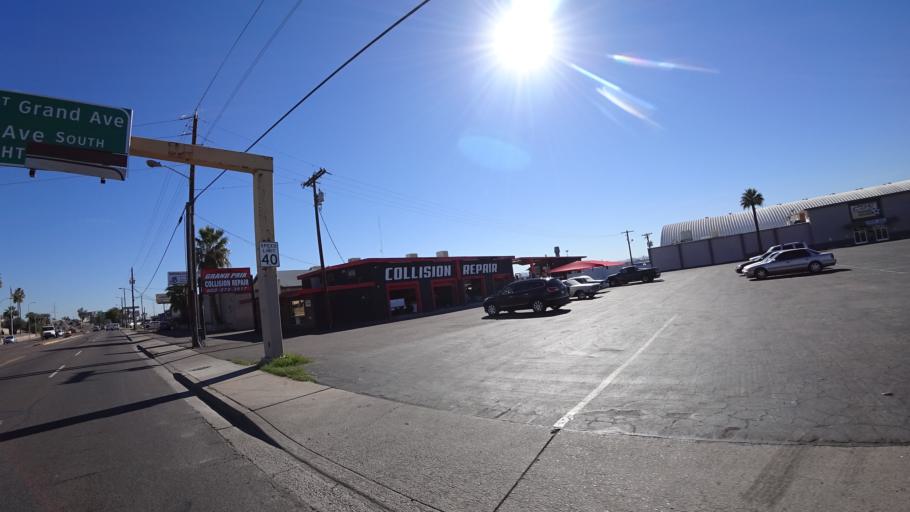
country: US
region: Arizona
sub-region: Maricopa County
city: Glendale
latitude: 33.4949
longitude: -112.1413
